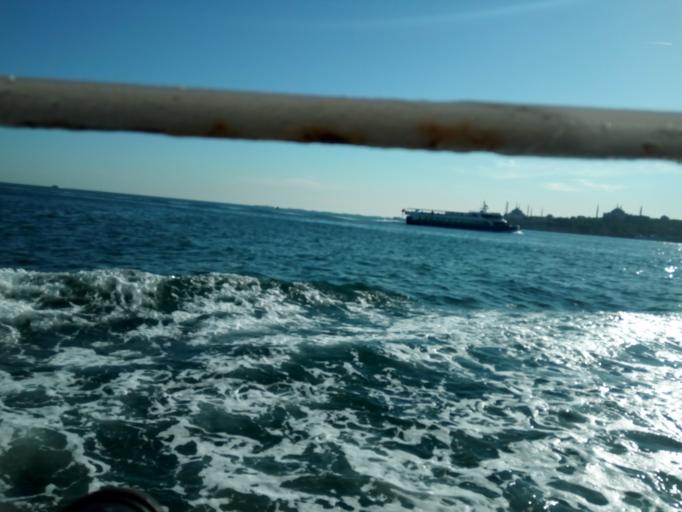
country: TR
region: Istanbul
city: UEskuedar
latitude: 41.0101
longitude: 29.0023
